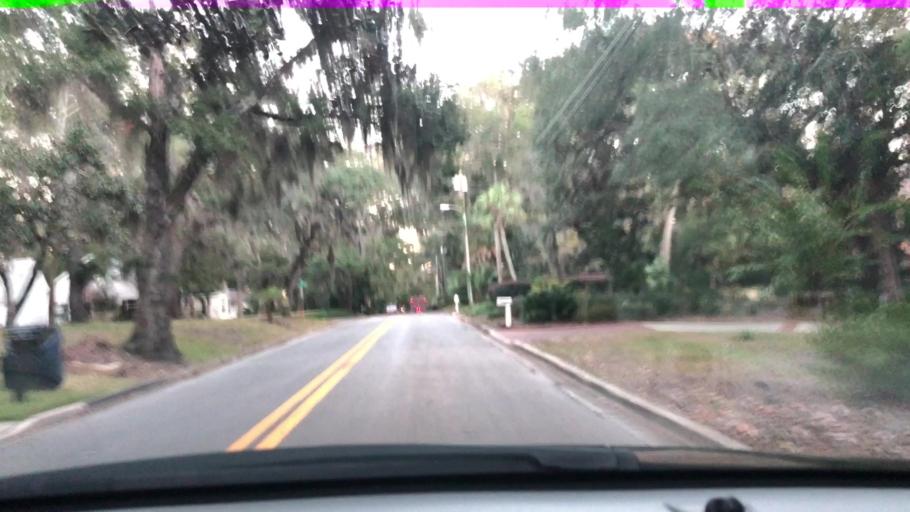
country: US
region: Florida
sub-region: Bay County
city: Panama City
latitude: 30.1353
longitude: -85.6403
